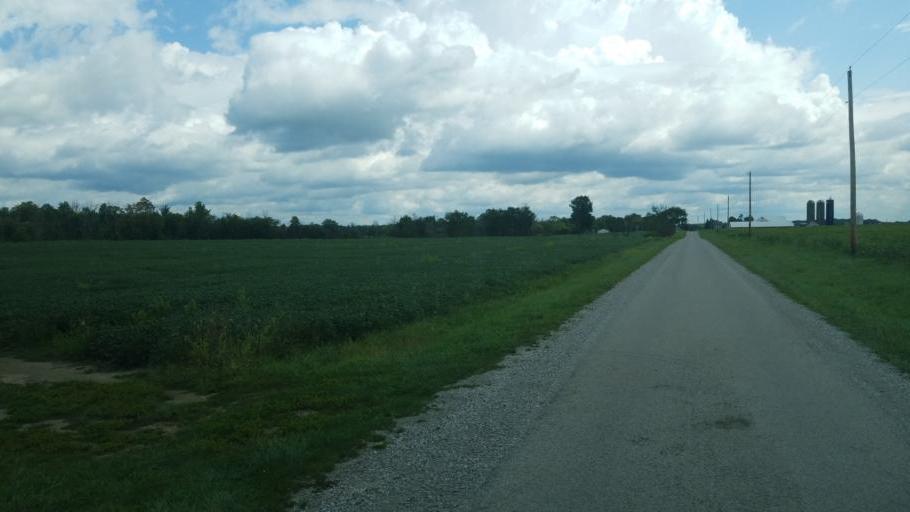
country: US
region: Ohio
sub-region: Huron County
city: Willard
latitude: 41.0952
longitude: -82.8657
